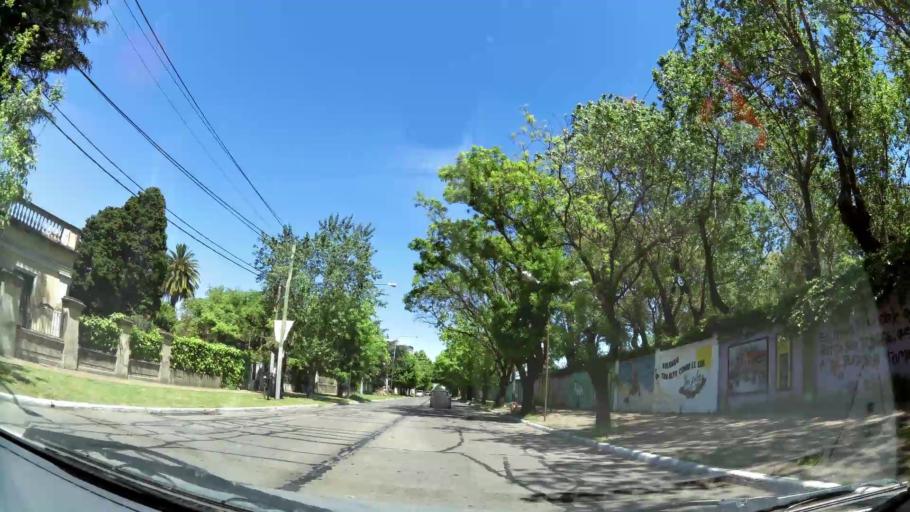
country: AR
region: Buenos Aires
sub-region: Partido de Quilmes
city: Quilmes
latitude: -34.7140
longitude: -58.2793
